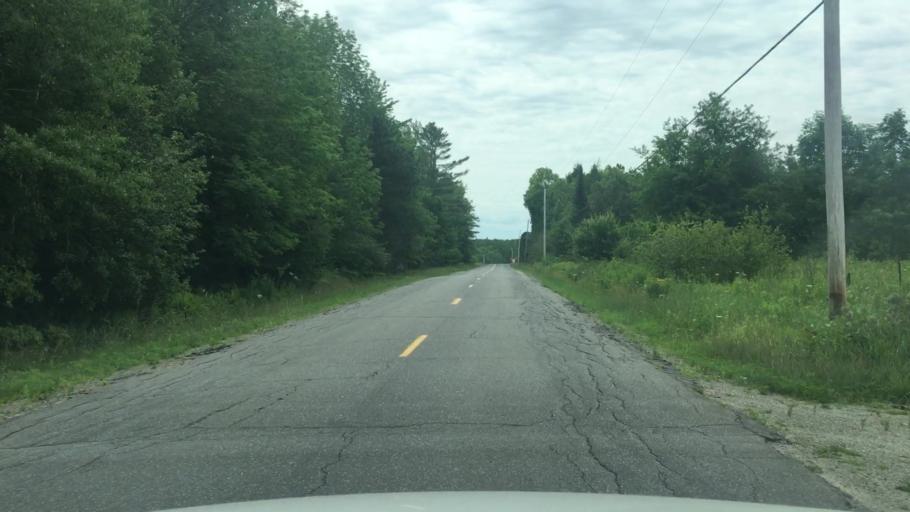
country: US
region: Maine
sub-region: Kennebec County
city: Albion
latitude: 44.4887
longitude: -69.3762
